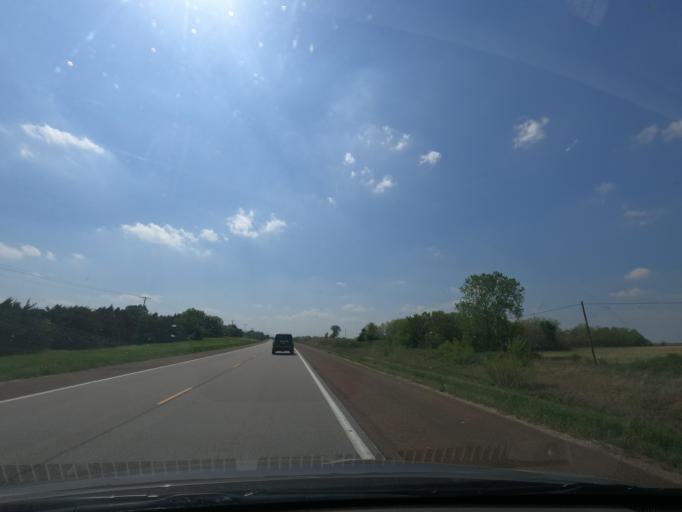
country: US
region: Kansas
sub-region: Butler County
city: El Dorado
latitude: 37.6797
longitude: -96.7964
